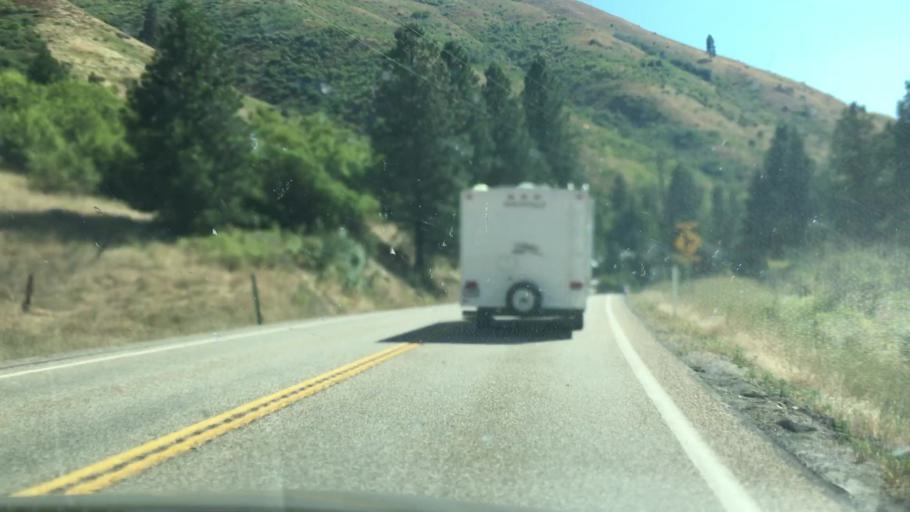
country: US
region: Idaho
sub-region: Boise County
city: Idaho City
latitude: 44.0286
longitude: -116.1348
